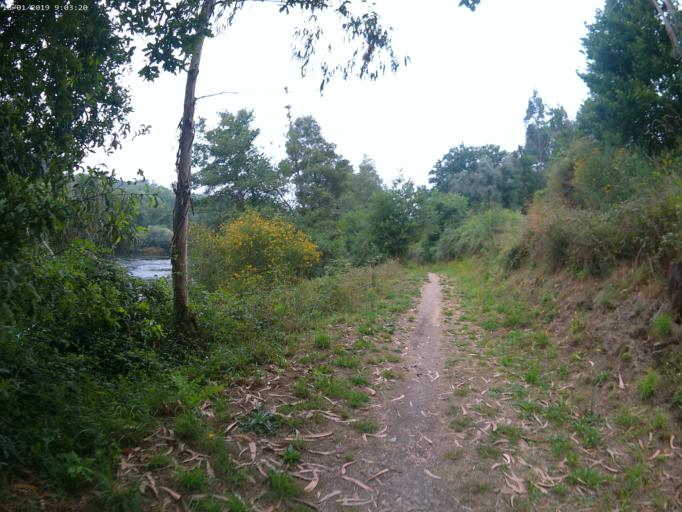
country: PT
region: Viana do Castelo
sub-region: Ponte da Barca
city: Ponte da Barca
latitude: 41.8058
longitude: -8.4429
